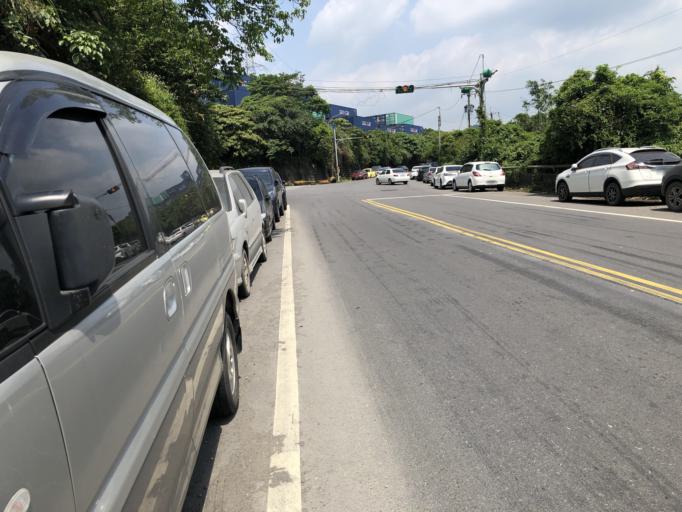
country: TW
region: Taiwan
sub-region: Keelung
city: Keelung
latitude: 25.0764
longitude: 121.6825
